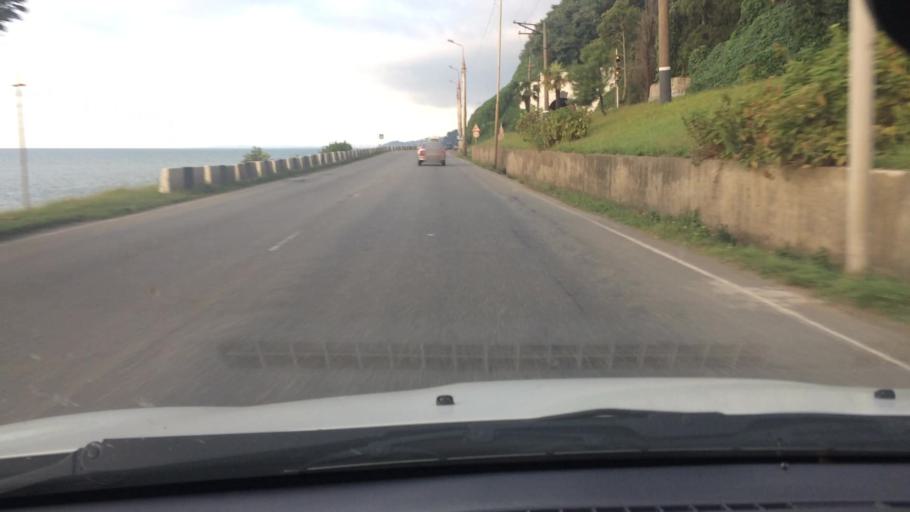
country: GE
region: Ajaria
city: Makhinjauri
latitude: 41.6695
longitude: 41.6878
